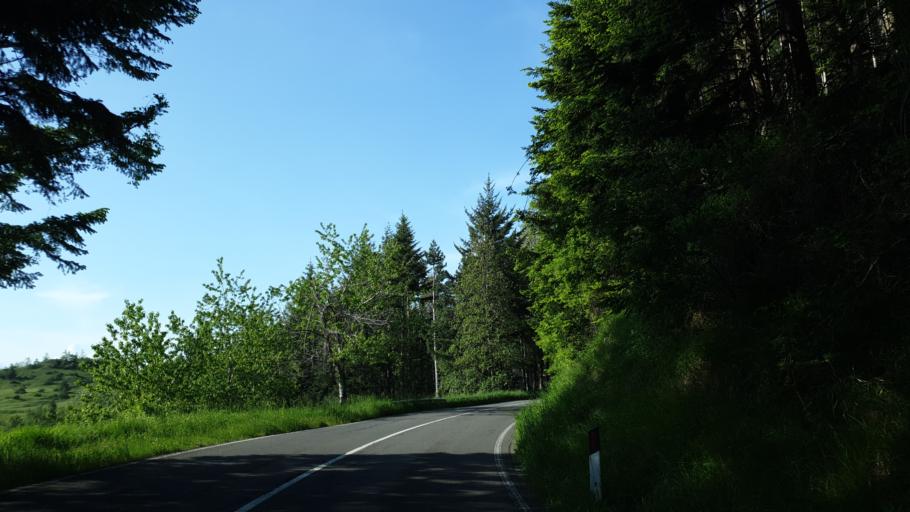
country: IT
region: Tuscany
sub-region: Province of Arezzo
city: Montemignaio
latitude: 43.7836
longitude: 11.6497
